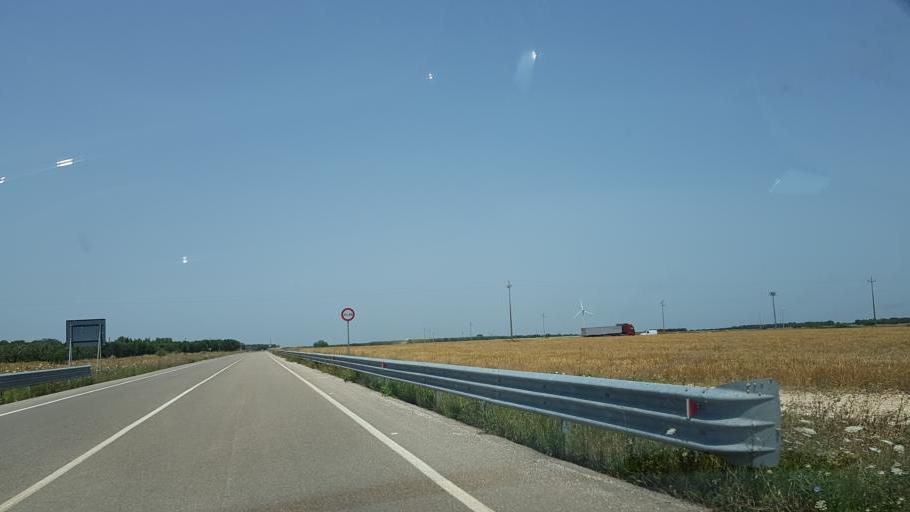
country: IT
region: Apulia
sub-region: Provincia di Brindisi
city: Mesagne
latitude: 40.5002
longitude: 17.8287
